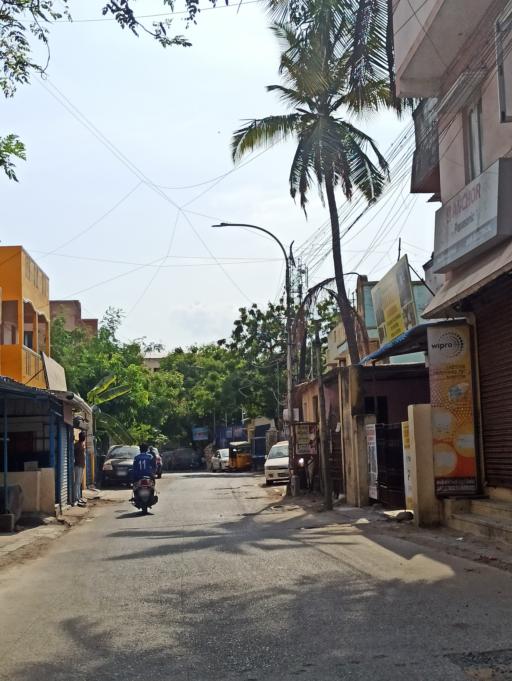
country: IN
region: Tamil Nadu
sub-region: Chennai
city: Chetput
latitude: 13.0583
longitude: 80.2151
